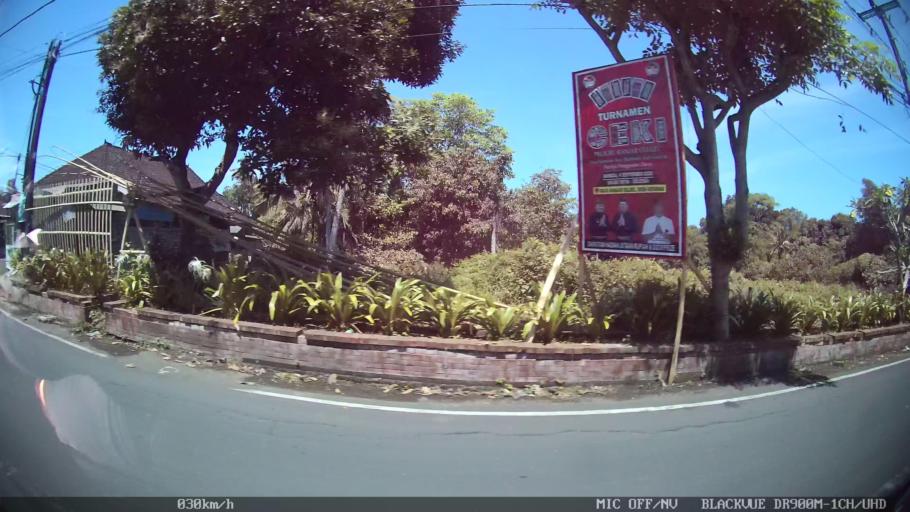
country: ID
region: Bali
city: Banjar Pasekan
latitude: -8.5713
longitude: 115.3276
